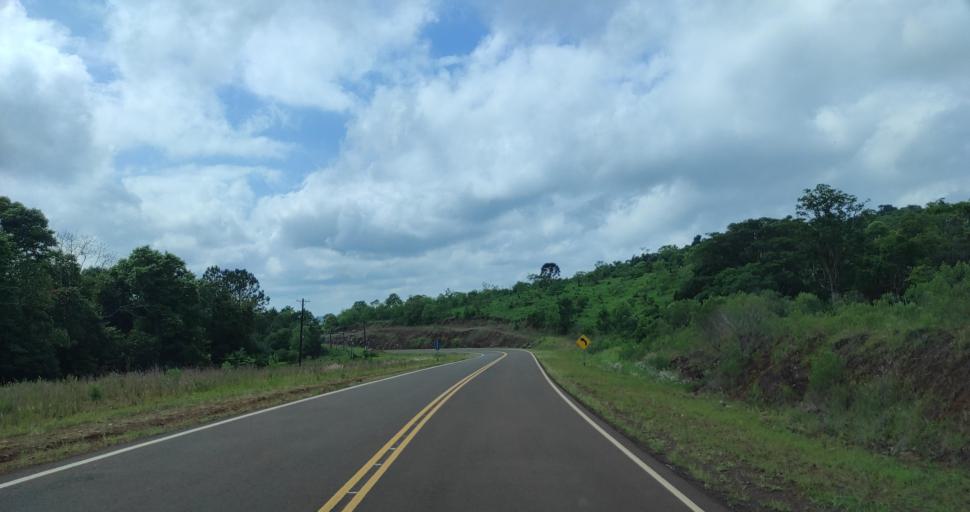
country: AR
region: Misiones
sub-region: Departamento de Veinticinco de Mayo
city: Veinticinco de Mayo
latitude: -27.3762
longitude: -54.8553
